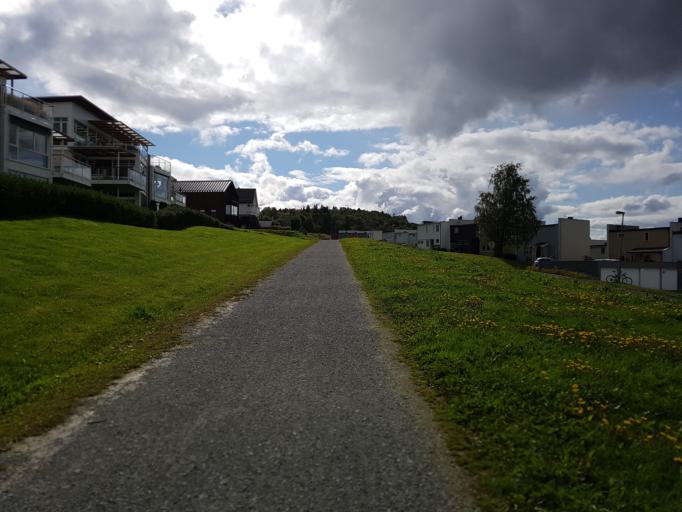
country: NO
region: Sor-Trondelag
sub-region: Trondheim
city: Trondheim
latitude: 63.4142
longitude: 10.4648
